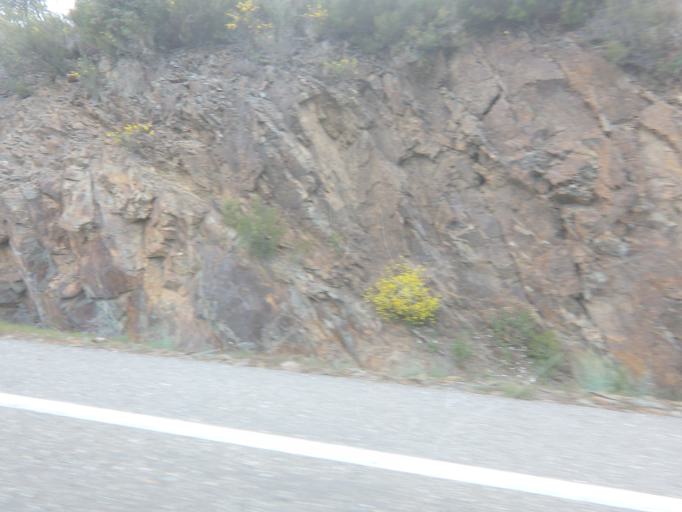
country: ES
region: Extremadura
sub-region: Provincia de Caceres
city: Acebo
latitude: 40.2427
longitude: -6.6852
